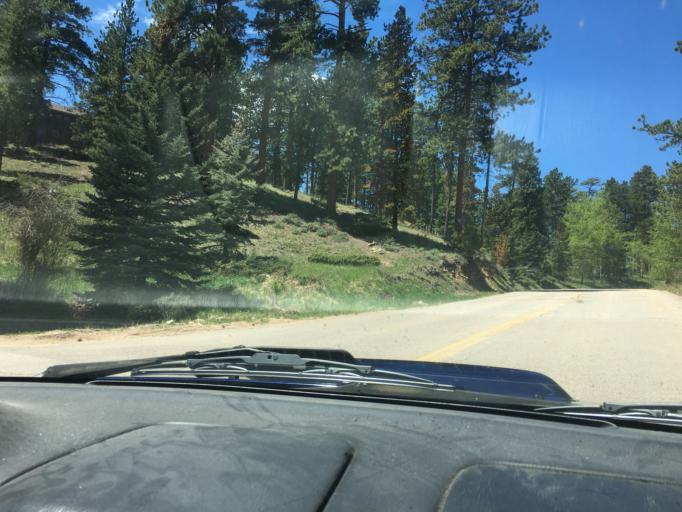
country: US
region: Colorado
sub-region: Larimer County
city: Estes Park
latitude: 40.3413
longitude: -105.5676
